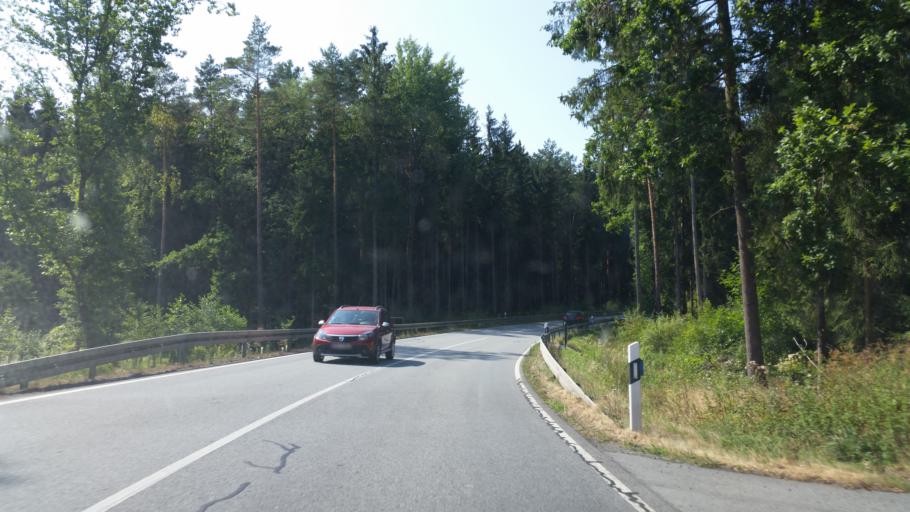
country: DE
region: Saxony
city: Grosshennersdorf
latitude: 50.9747
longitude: 14.7537
